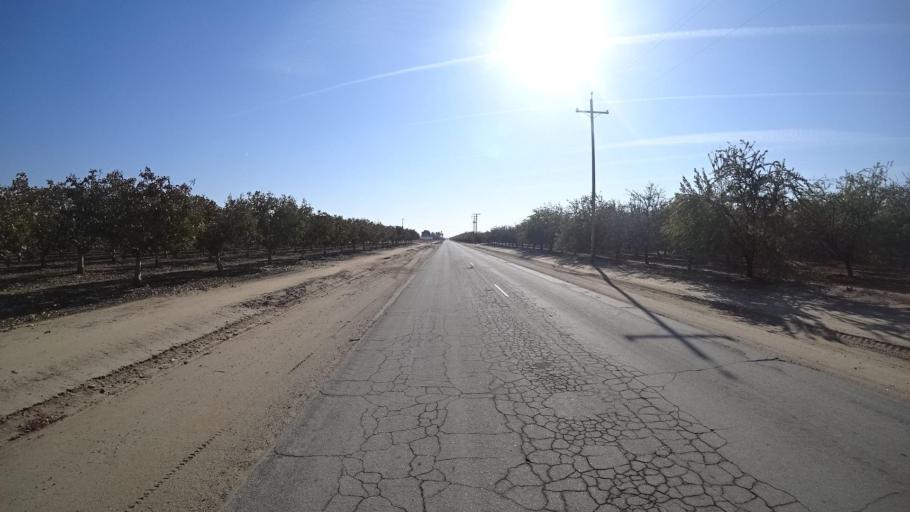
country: US
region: California
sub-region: Kern County
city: Wasco
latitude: 35.6571
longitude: -119.3486
